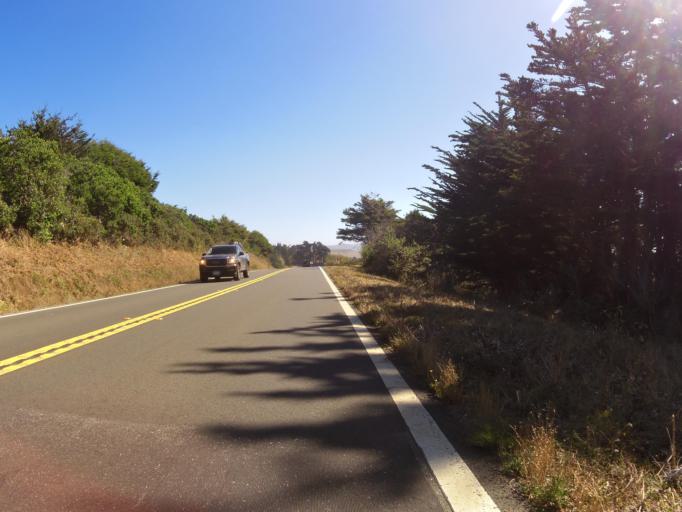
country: US
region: California
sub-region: Mendocino County
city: Fort Bragg
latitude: 39.5944
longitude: -123.7816
